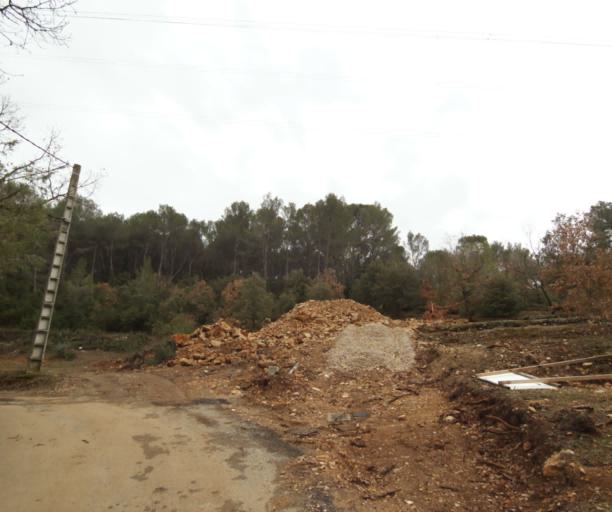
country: FR
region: Provence-Alpes-Cote d'Azur
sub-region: Departement du Var
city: Trans-en-Provence
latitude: 43.5141
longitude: 6.4838
